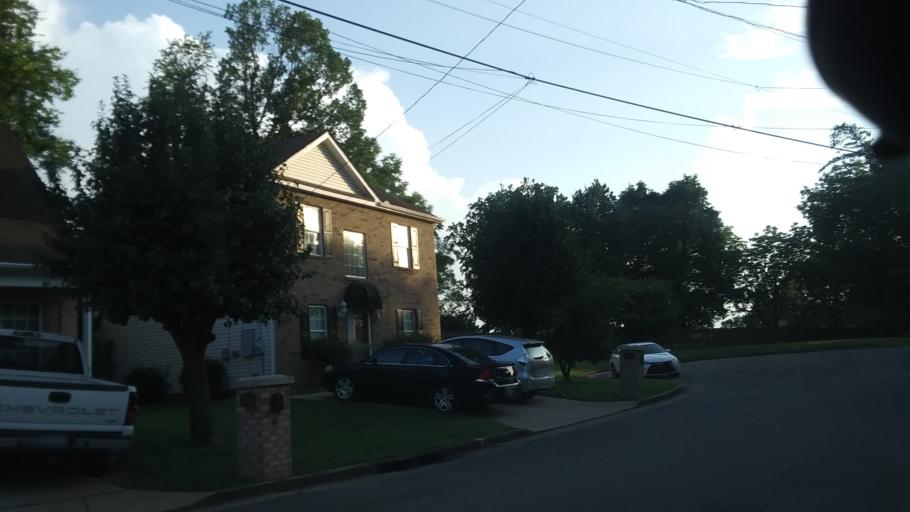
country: US
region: Tennessee
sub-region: Davidson County
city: Belle Meade
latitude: 36.1567
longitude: -86.8761
